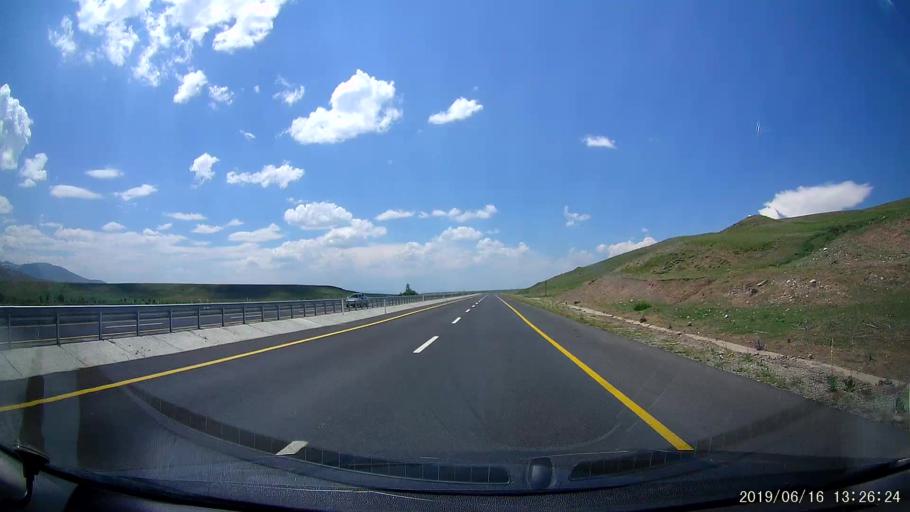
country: TR
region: Agri
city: Taslicay
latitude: 39.6588
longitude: 43.3293
